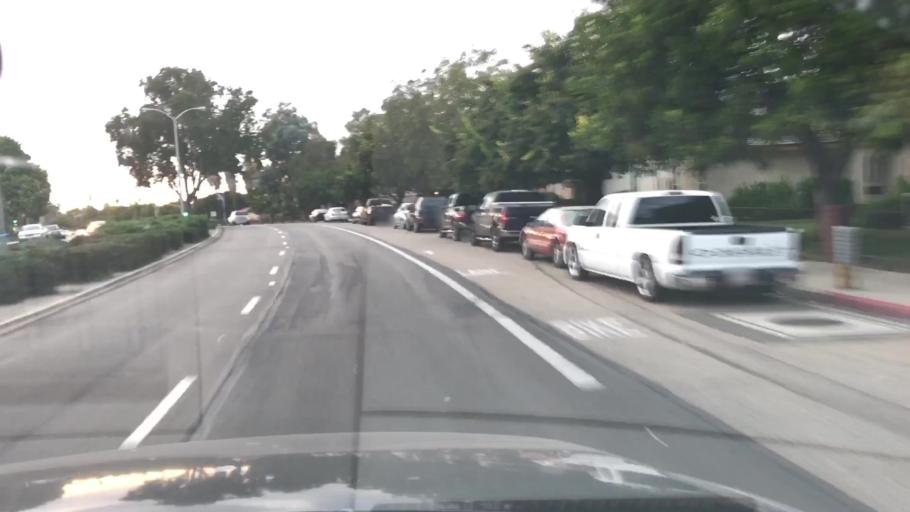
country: US
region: California
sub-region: Ventura County
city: El Rio
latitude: 34.2291
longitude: -119.1843
